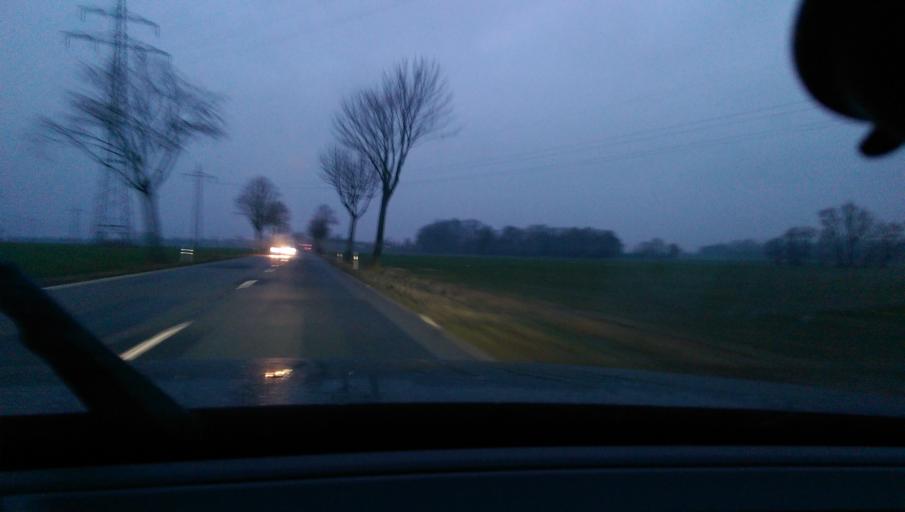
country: DE
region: Lower Saxony
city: Grossgoltern
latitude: 52.3482
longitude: 9.5491
